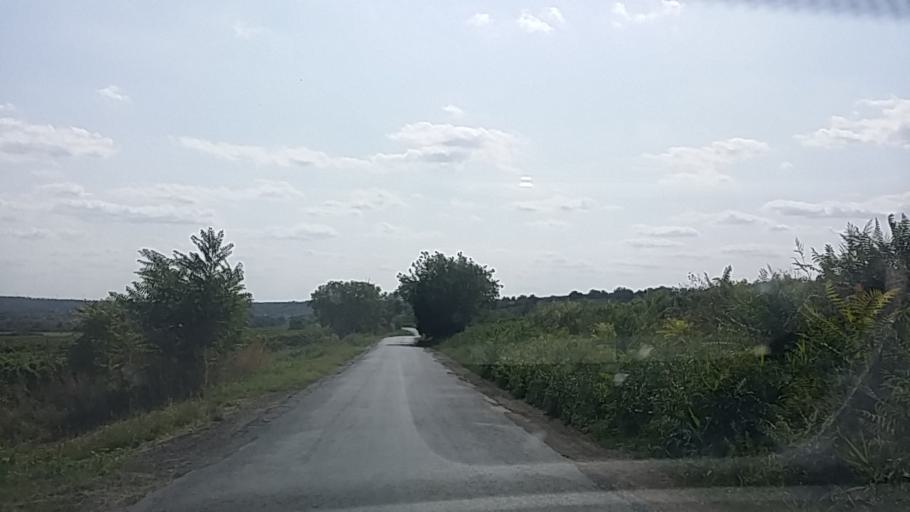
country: HU
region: Gyor-Moson-Sopron
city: Fertorakos
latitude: 47.6677
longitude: 16.6704
